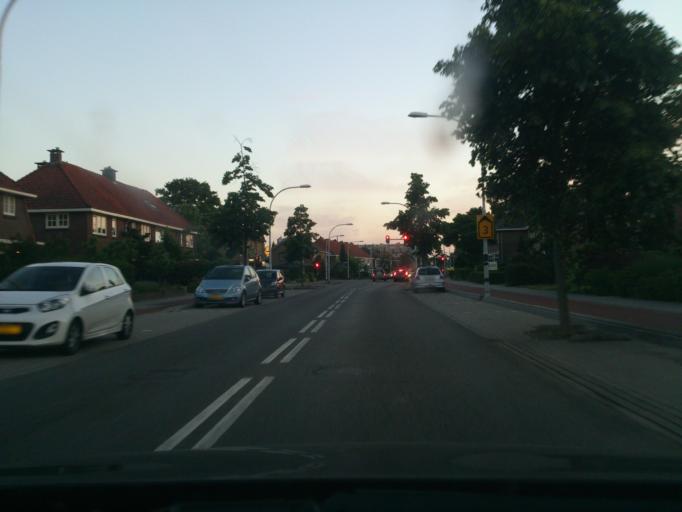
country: NL
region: Gelderland
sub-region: Gemeente Nijmegen
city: Nijmegen
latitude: 51.8102
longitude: 5.8290
